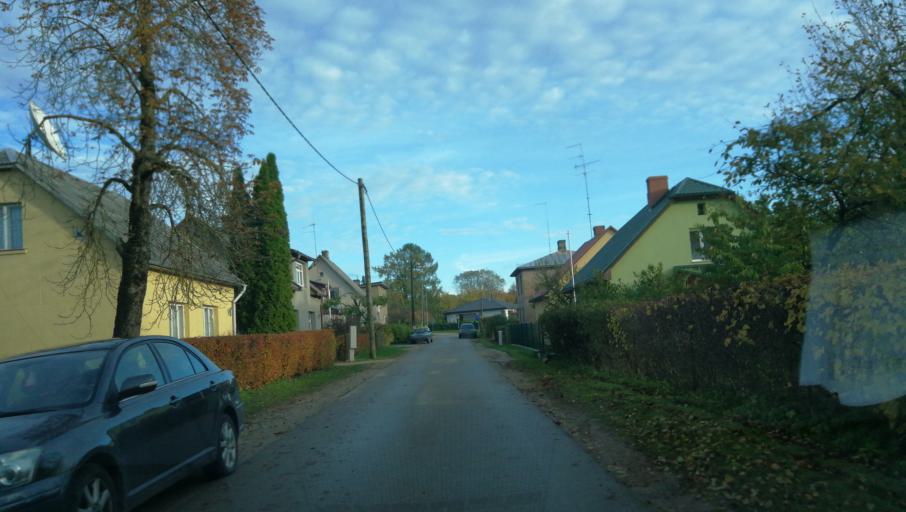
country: LV
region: Cesu Rajons
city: Cesis
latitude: 57.3038
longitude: 25.2631
